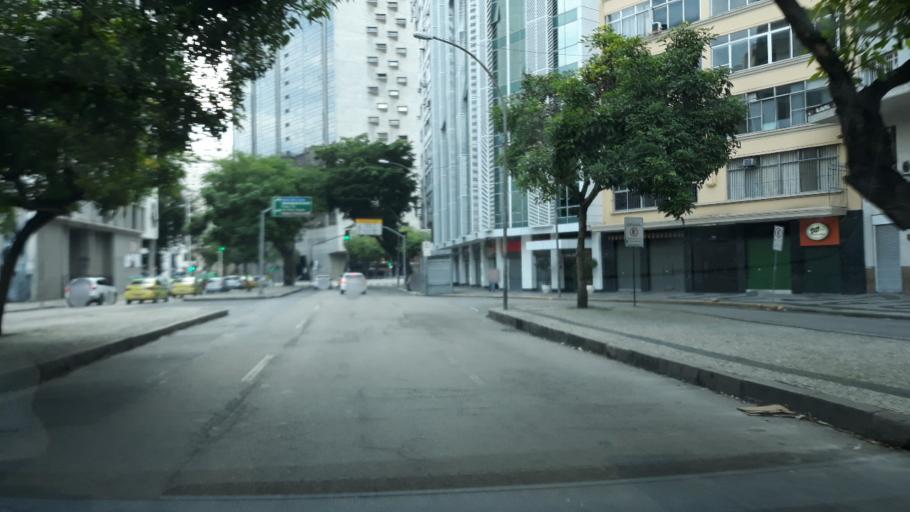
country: BR
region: Rio de Janeiro
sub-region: Rio De Janeiro
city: Rio de Janeiro
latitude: -22.9095
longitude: -43.1707
